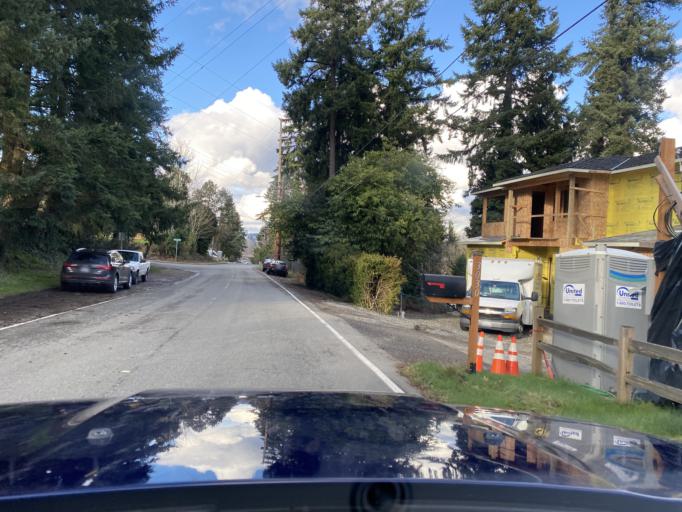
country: US
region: Washington
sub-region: King County
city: Newport
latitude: 47.5829
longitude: -122.1912
